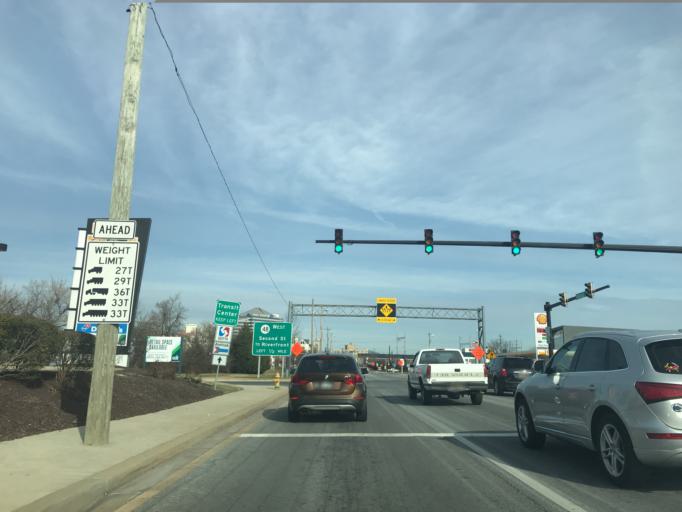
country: US
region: Delaware
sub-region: New Castle County
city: Wilmington
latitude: 39.7320
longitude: -75.5533
